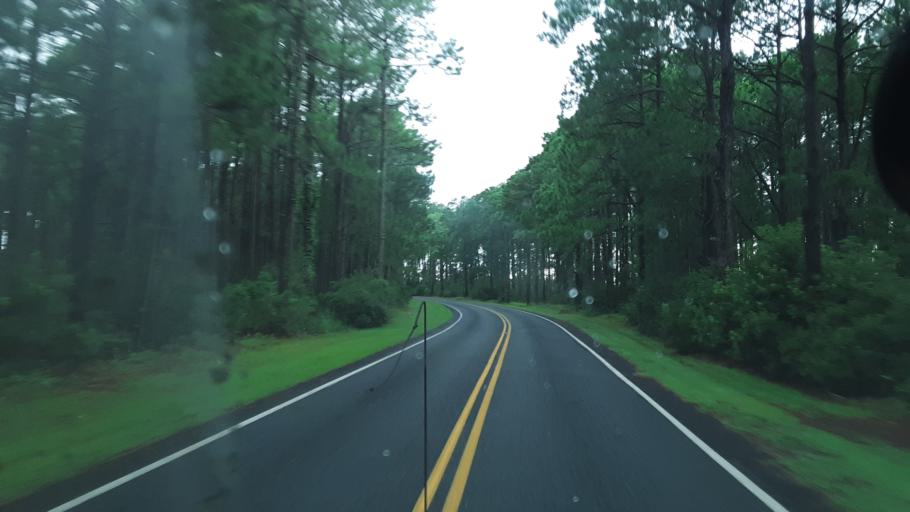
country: US
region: North Carolina
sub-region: Dare County
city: Wanchese
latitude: 35.8270
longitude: -75.5613
